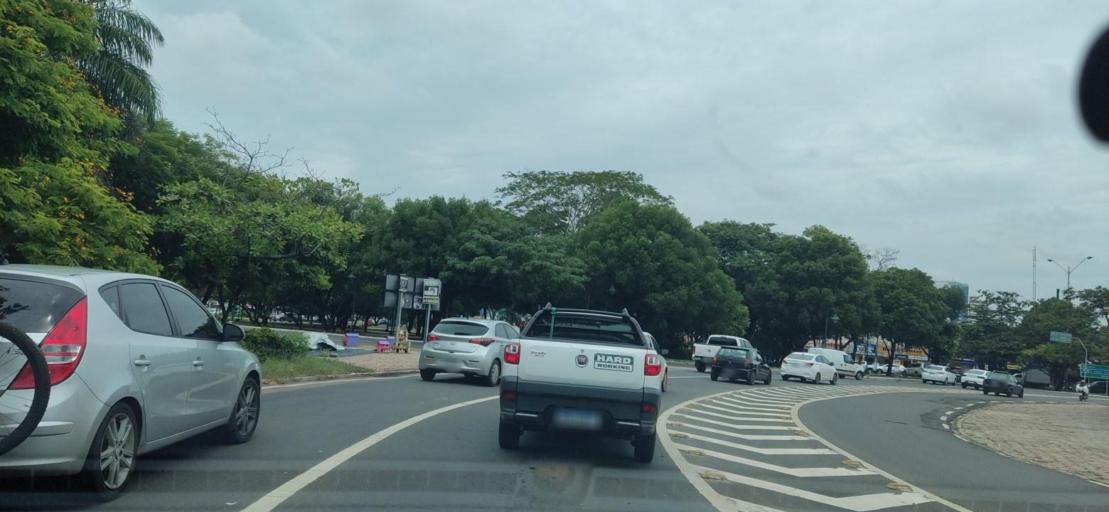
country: BR
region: Piaui
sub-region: Teresina
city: Teresina
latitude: -5.0812
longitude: -42.7741
